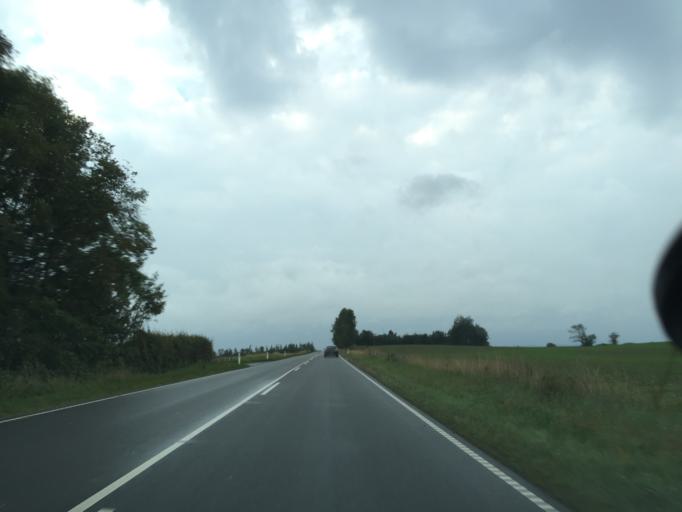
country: DK
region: Central Jutland
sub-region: Skanderborg Kommune
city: Skanderborg
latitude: 56.0792
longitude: 9.8988
